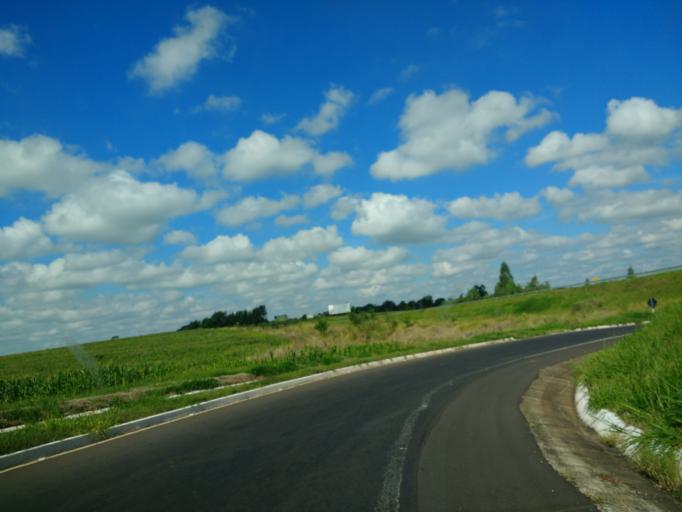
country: BR
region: Parana
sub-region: Alto Piquiri
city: Alto Piquiri
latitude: -23.8902
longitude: -53.4644
